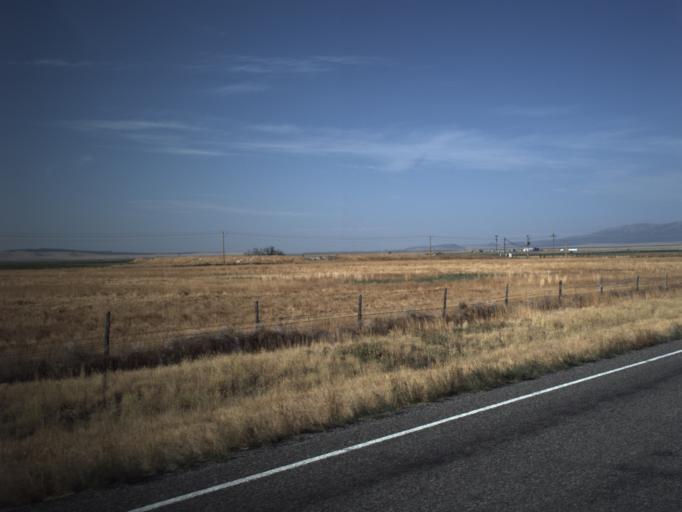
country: US
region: Idaho
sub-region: Oneida County
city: Malad City
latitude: 41.9665
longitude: -112.9173
